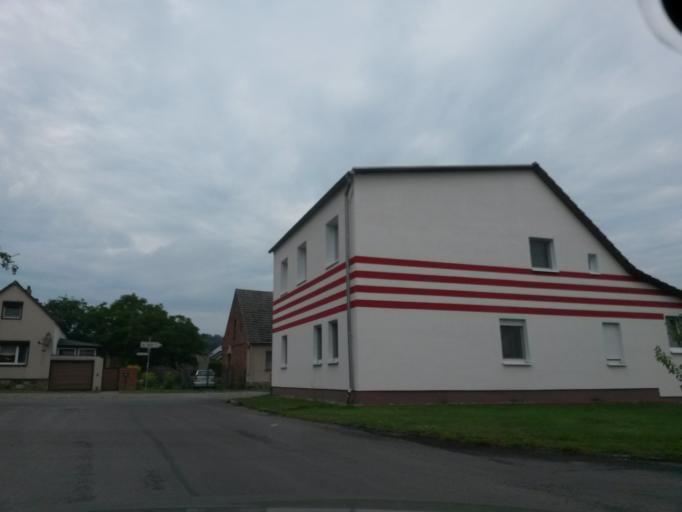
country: DE
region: Brandenburg
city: Chorin
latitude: 52.9030
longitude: 13.8724
